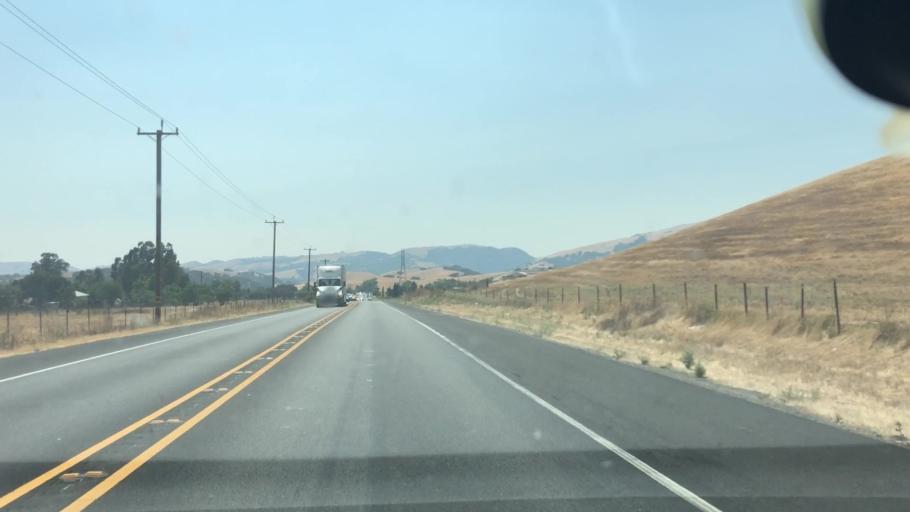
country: US
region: California
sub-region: Alameda County
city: Pleasanton
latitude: 37.6057
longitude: -121.8362
